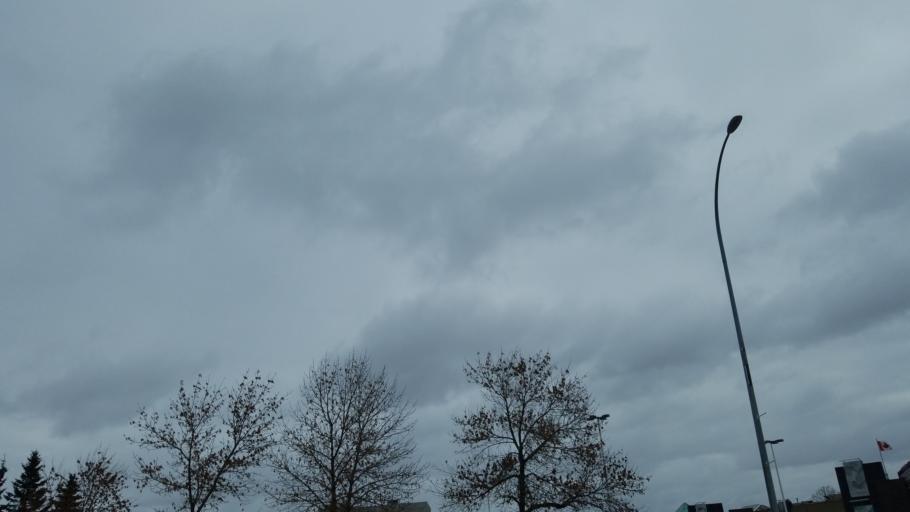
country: CA
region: Alberta
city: Sherwood Park
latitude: 53.5324
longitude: -113.2957
